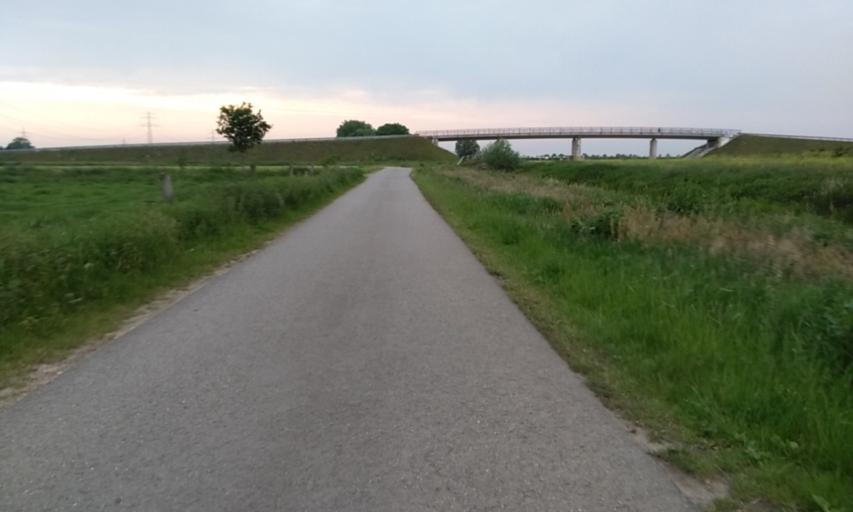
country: DE
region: Lower Saxony
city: Buxtehude
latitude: 53.4954
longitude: 9.6820
